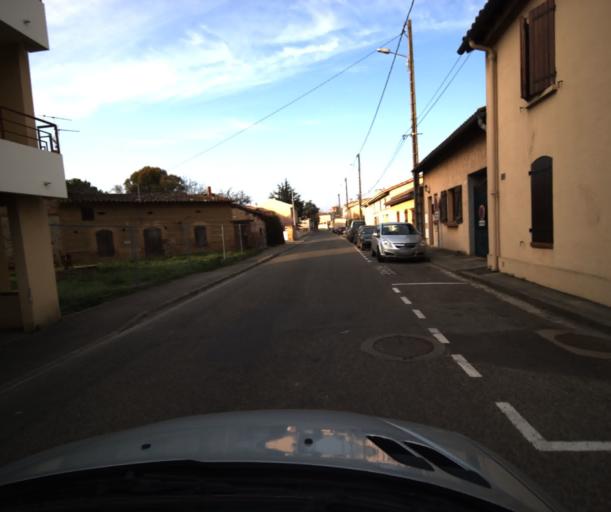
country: FR
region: Midi-Pyrenees
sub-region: Departement de la Haute-Garonne
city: Castelginest
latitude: 43.6915
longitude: 1.4320
